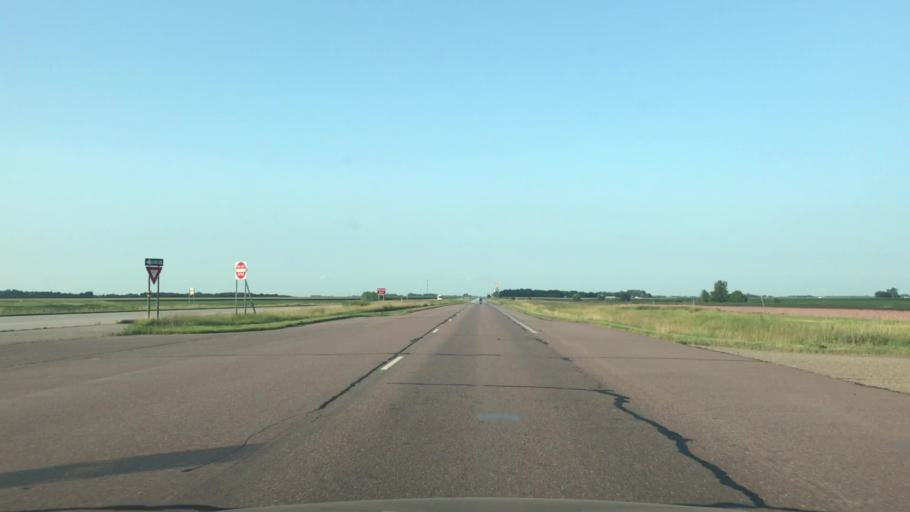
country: US
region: Minnesota
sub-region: Jackson County
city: Lakefield
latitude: 43.7470
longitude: -95.3969
